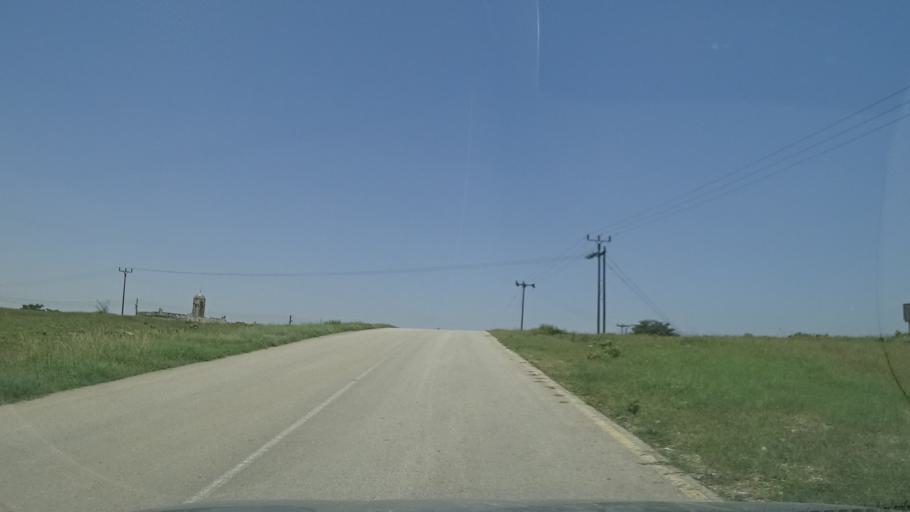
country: OM
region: Zufar
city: Salalah
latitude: 17.2484
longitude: 54.2635
